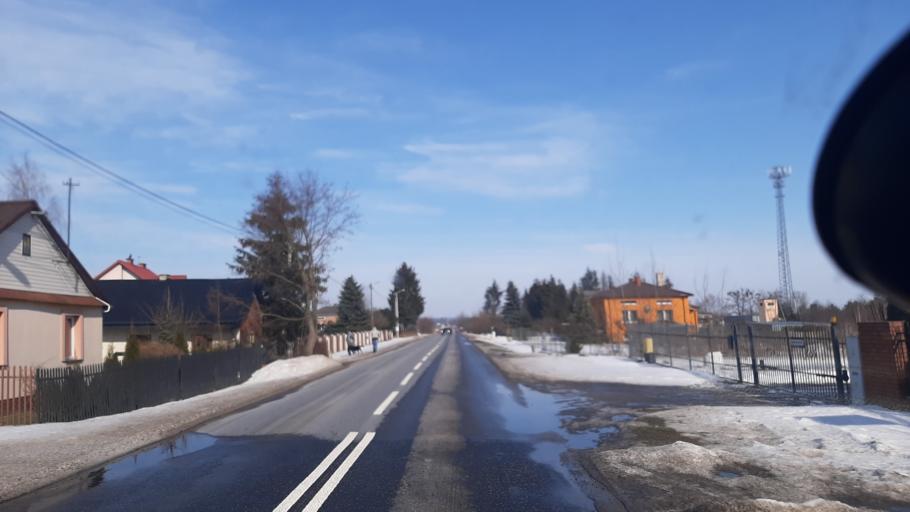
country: PL
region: Lublin Voivodeship
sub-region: Powiat pulawski
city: Kurow
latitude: 51.3970
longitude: 22.1982
